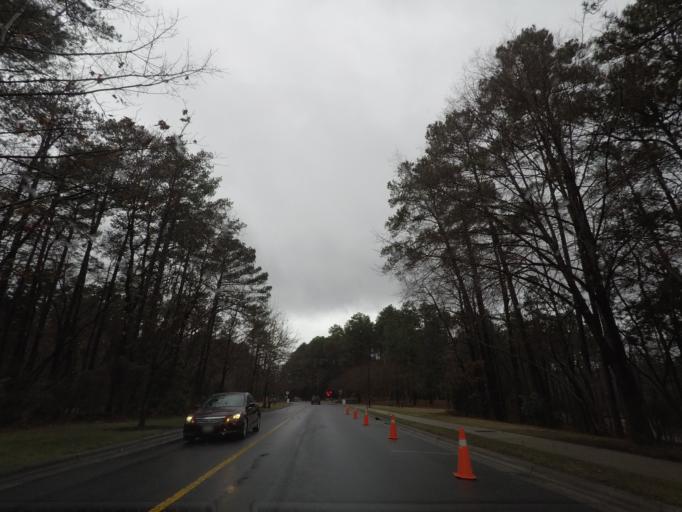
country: US
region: North Carolina
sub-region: Durham County
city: Durham
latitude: 36.0011
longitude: -78.9463
